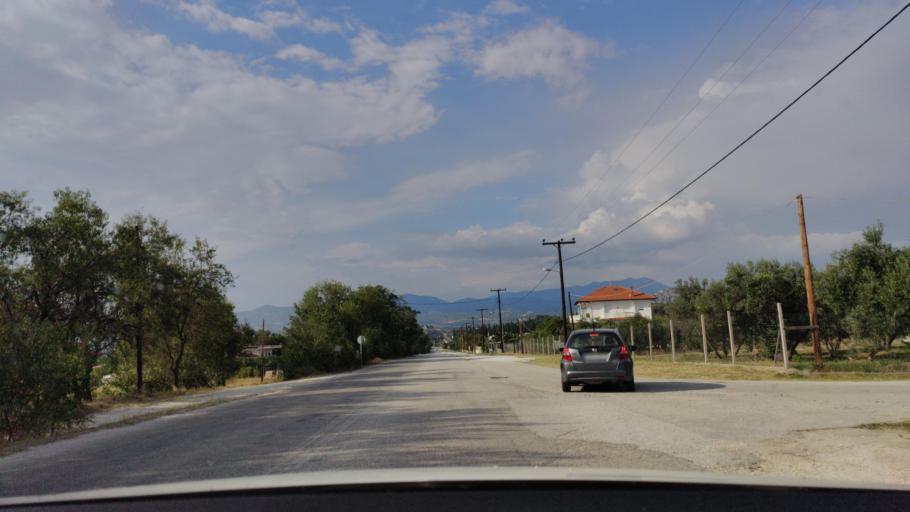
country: GR
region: Central Macedonia
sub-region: Nomos Serron
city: Sidirokastro
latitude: 41.2211
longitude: 23.3900
